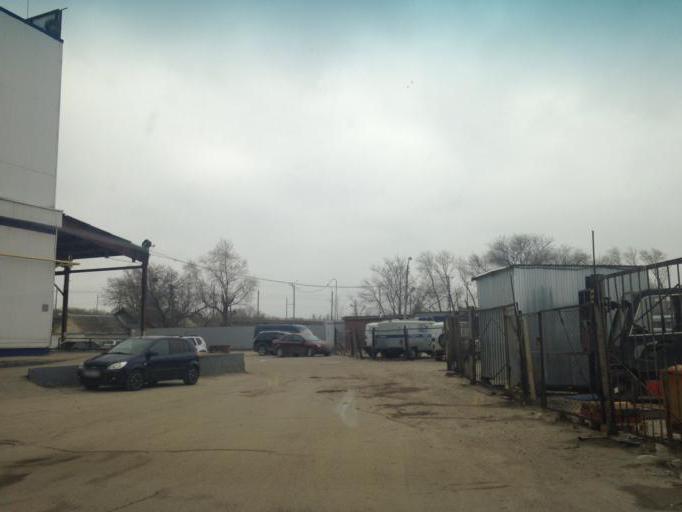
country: RU
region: Ulyanovsk
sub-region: Ulyanovskiy Rayon
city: Ulyanovsk
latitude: 54.3061
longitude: 48.3066
